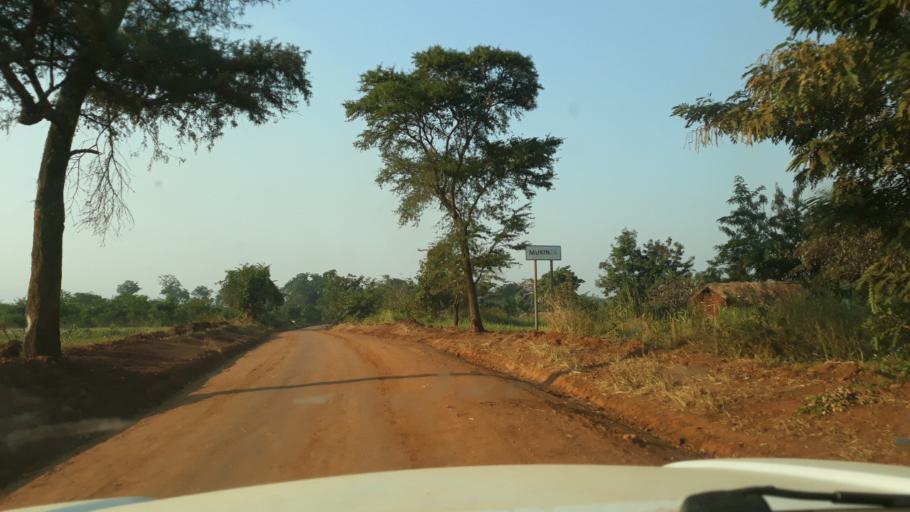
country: BI
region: Bururi
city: Rumonge
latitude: -4.2277
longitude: 28.9928
